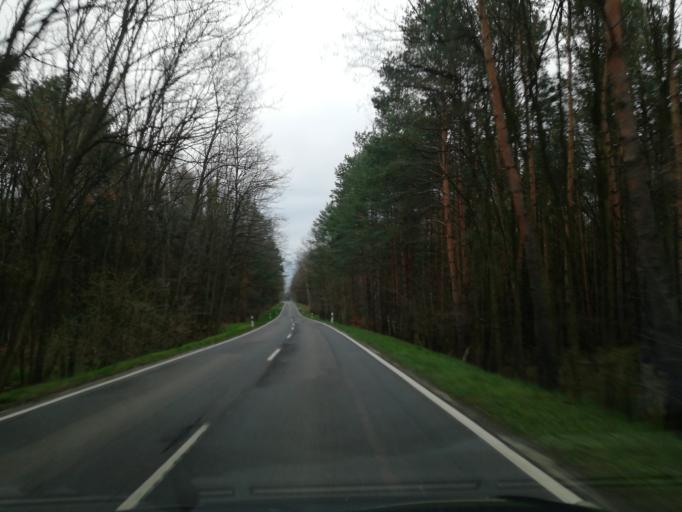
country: DE
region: Brandenburg
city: Vetschau
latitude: 51.7670
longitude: 14.0650
